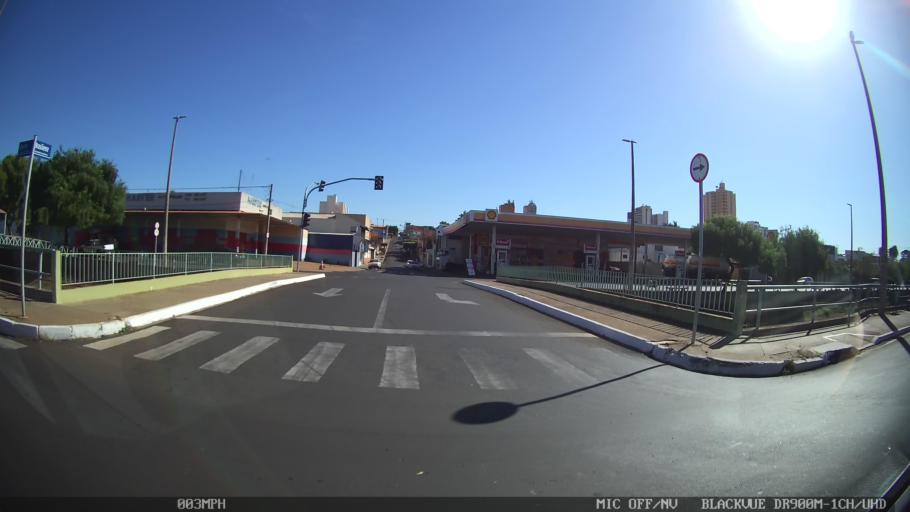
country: BR
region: Sao Paulo
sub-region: Olimpia
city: Olimpia
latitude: -20.7393
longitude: -48.9102
